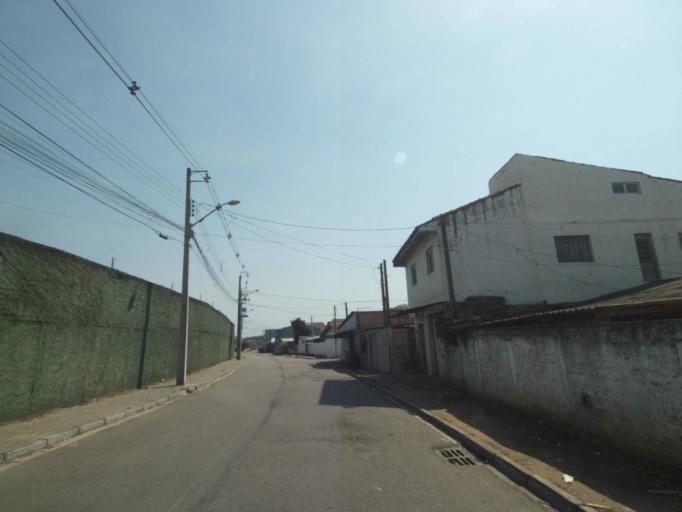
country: BR
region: Parana
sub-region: Curitiba
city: Curitiba
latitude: -25.4821
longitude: -49.3034
